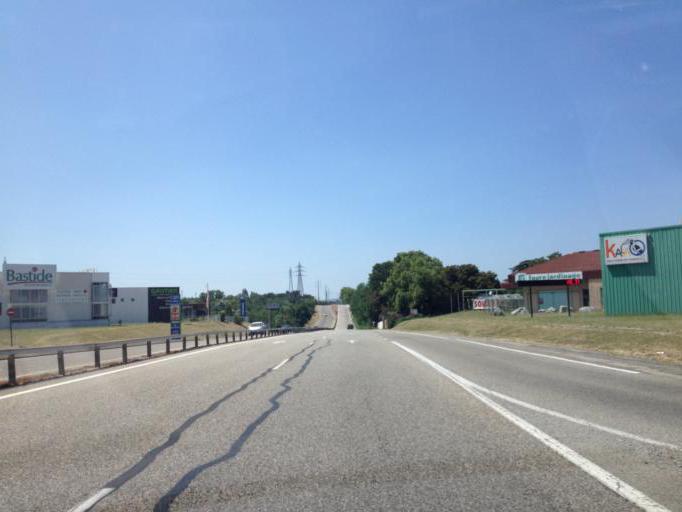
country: FR
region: Rhone-Alpes
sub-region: Departement de la Drome
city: Bourg-les-Valence
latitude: 44.9502
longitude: 4.9274
